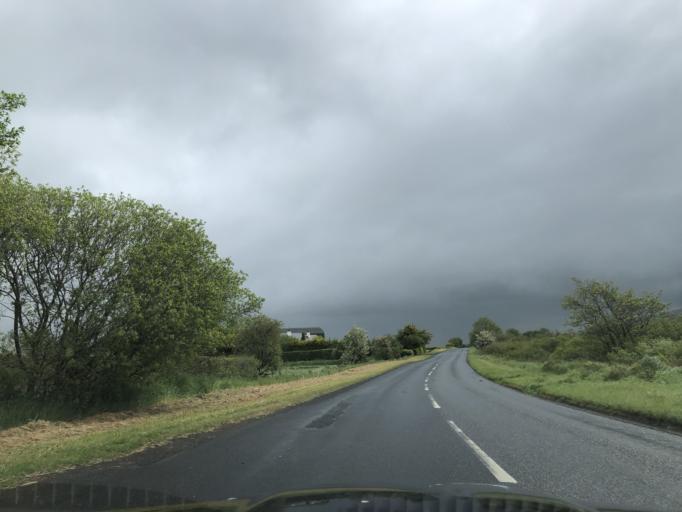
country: GB
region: Northern Ireland
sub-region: Moyle District
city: Ballycastle
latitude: 55.1691
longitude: -6.3557
